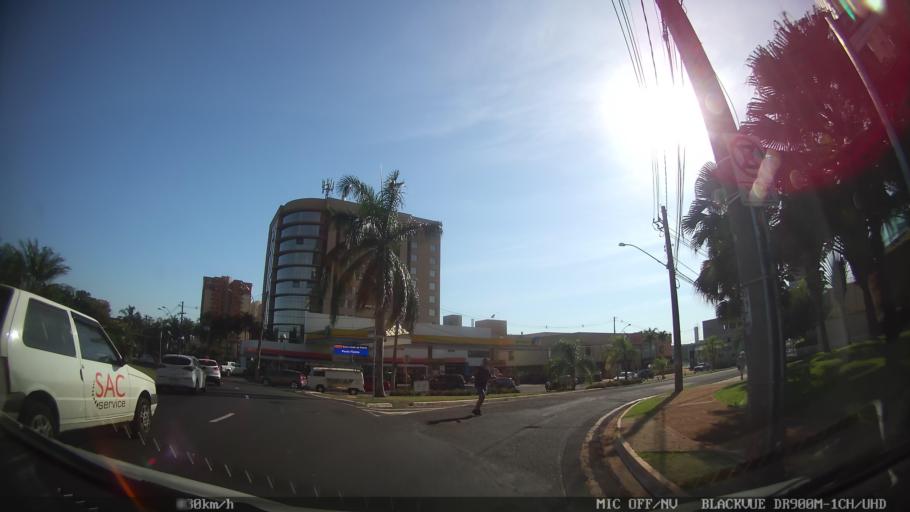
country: BR
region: Sao Paulo
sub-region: Ribeirao Preto
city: Ribeirao Preto
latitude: -21.2122
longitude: -47.8050
